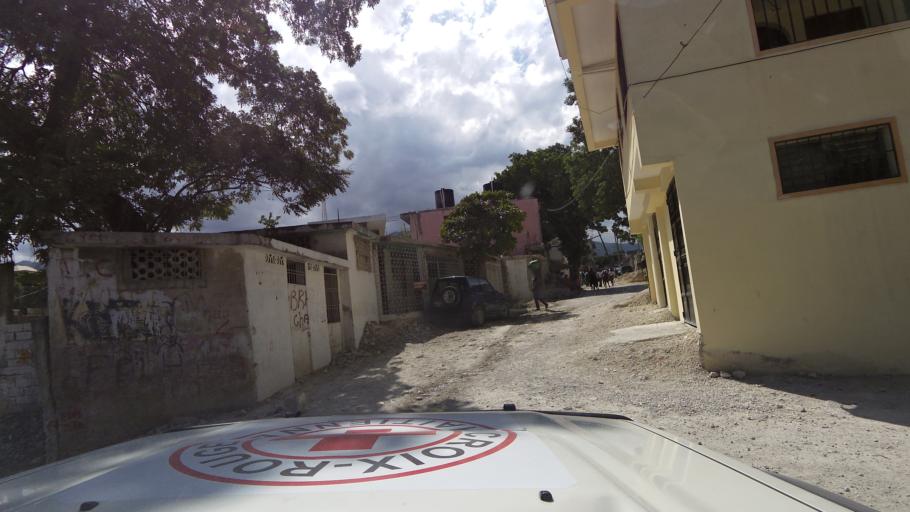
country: HT
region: Ouest
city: Delmas 73
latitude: 18.5430
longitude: -72.2983
